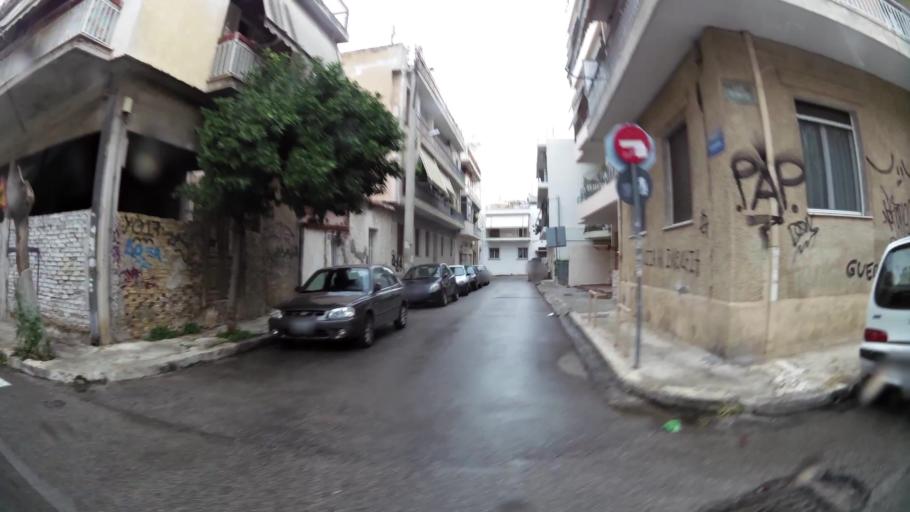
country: GR
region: Attica
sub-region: Nomarchia Athinas
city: Vyronas
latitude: 37.9570
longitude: 23.7516
